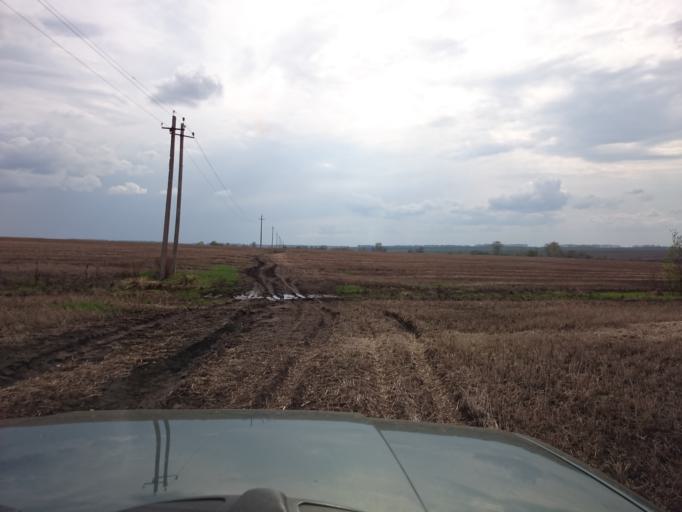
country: RU
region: Mordoviya
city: Kadoshkino
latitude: 54.0207
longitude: 44.4694
